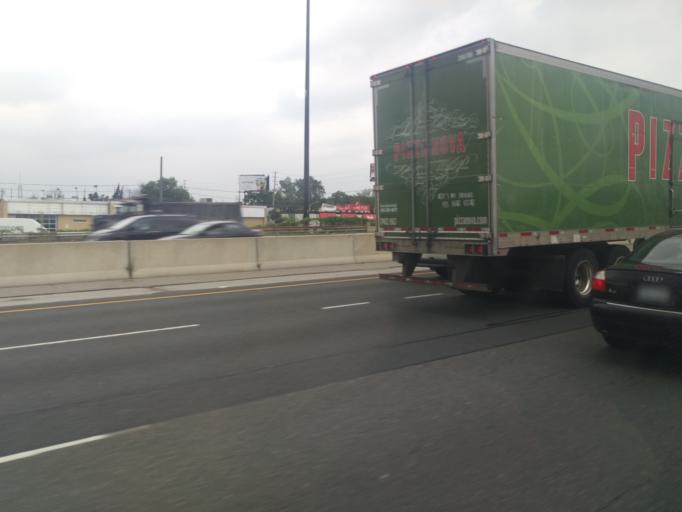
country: CA
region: Ontario
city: Etobicoke
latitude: 43.6156
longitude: -79.5370
